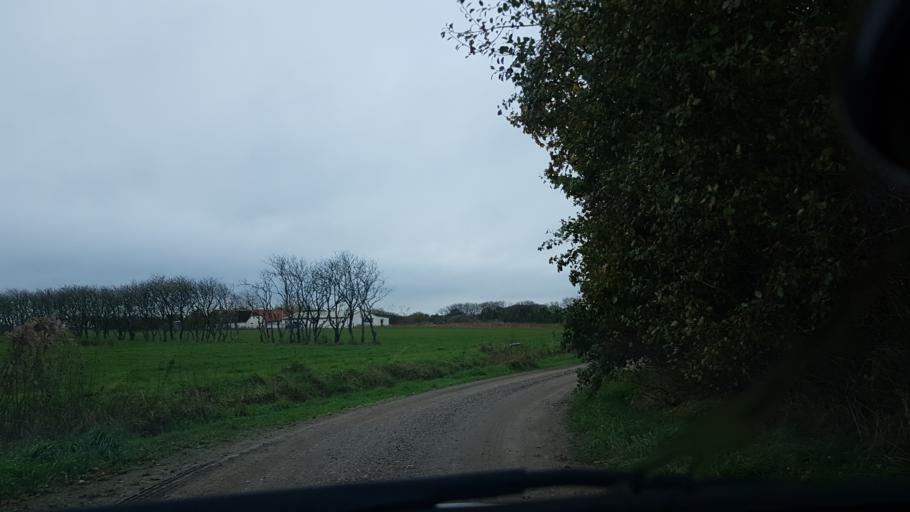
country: DK
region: South Denmark
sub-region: Esbjerg Kommune
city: Ribe
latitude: 55.2795
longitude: 8.8538
